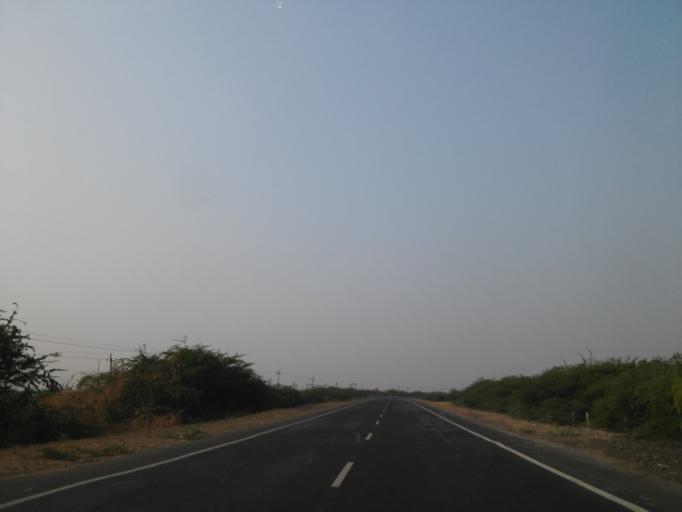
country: IN
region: Gujarat
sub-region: Kachchh
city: Anjar
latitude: 23.2940
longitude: 70.0971
